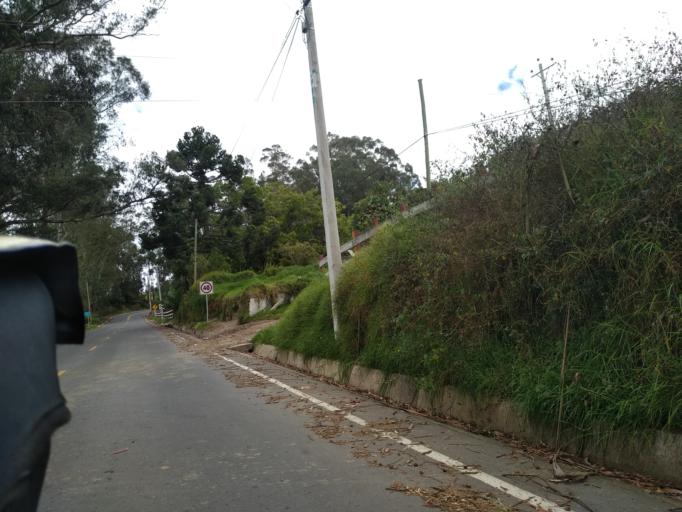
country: EC
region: Cotopaxi
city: Saquisili
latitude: -0.7193
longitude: -78.8877
